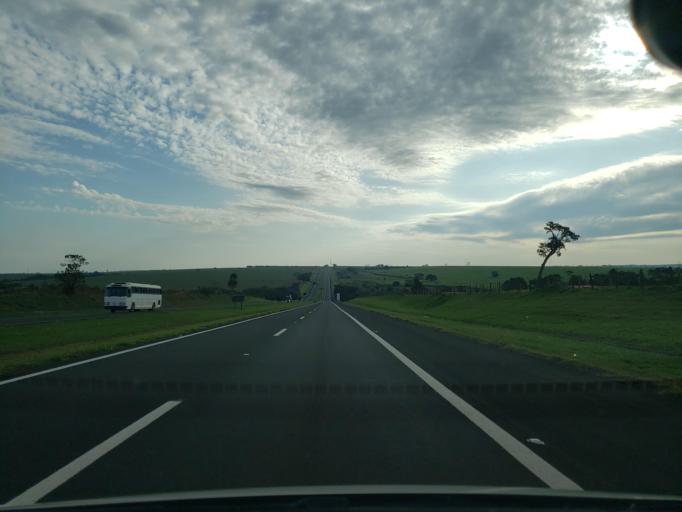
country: BR
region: Sao Paulo
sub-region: Guararapes
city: Guararapes
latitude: -21.2098
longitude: -50.7354
